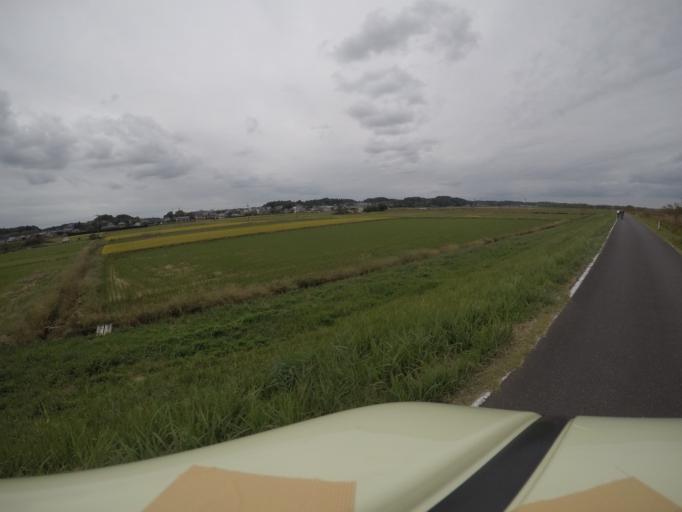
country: JP
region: Ibaraki
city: Ami
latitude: 36.0344
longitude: 140.2754
